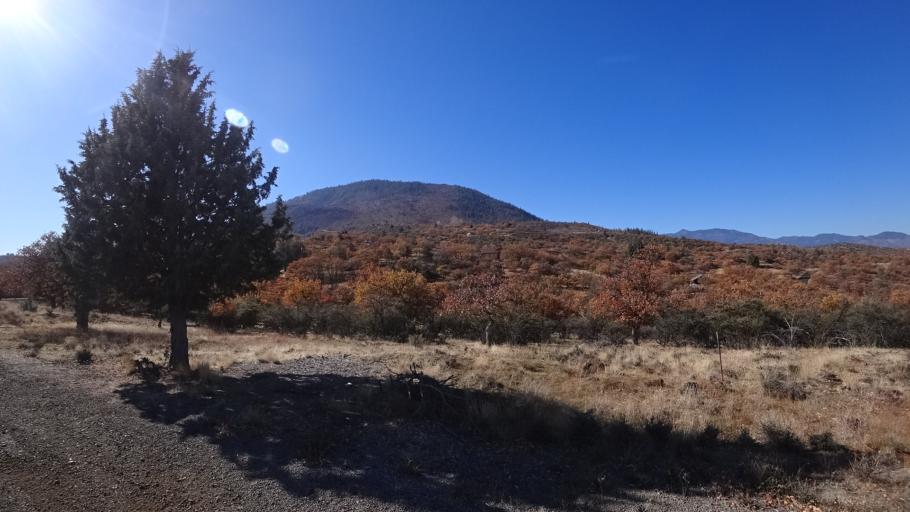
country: US
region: California
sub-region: Siskiyou County
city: Montague
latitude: 41.8769
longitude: -122.4853
